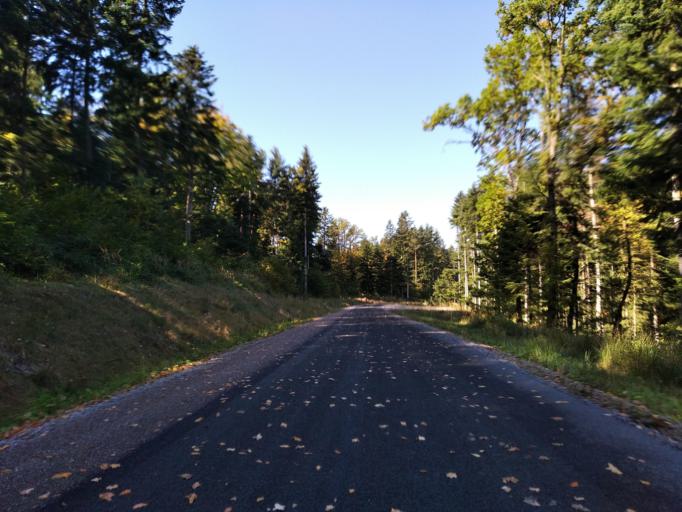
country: PL
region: Subcarpathian Voivodeship
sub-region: Powiat strzyzowski
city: Strzyzow
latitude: 49.8214
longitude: 21.8031
